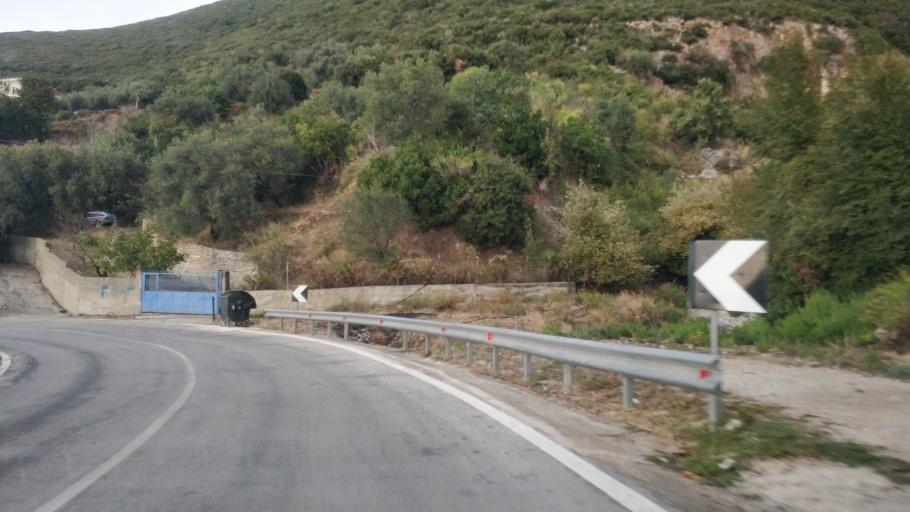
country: AL
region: Vlore
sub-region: Rrethi i Sarandes
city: Lukove
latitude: 40.0530
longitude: 19.8702
